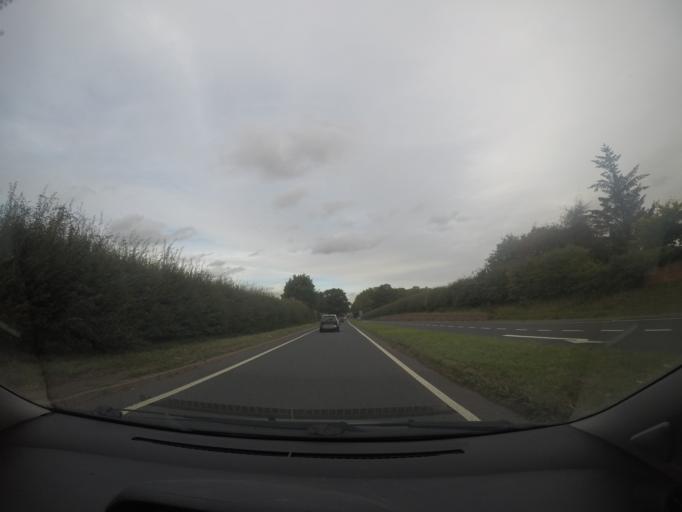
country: GB
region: England
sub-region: City of York
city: Deighton
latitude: 53.8712
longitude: -1.0486
